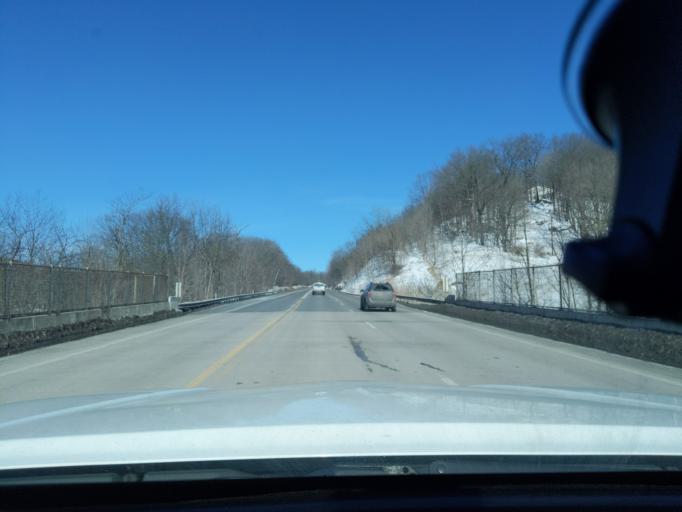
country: US
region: Maryland
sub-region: Allegany County
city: Westernport
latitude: 39.5270
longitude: -79.0162
